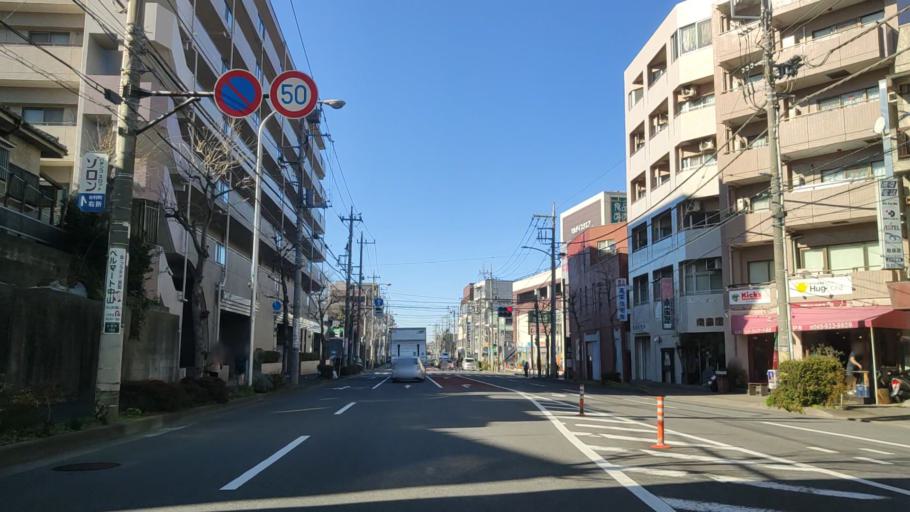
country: JP
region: Tokyo
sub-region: Machida-shi
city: Machida
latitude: 35.5137
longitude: 139.5375
